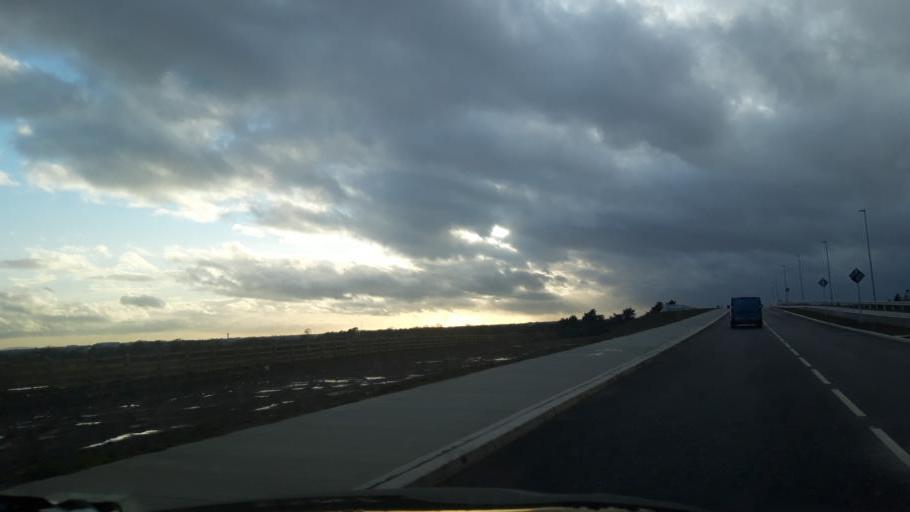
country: IE
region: Leinster
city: Donabate
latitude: 53.4792
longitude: -6.1490
